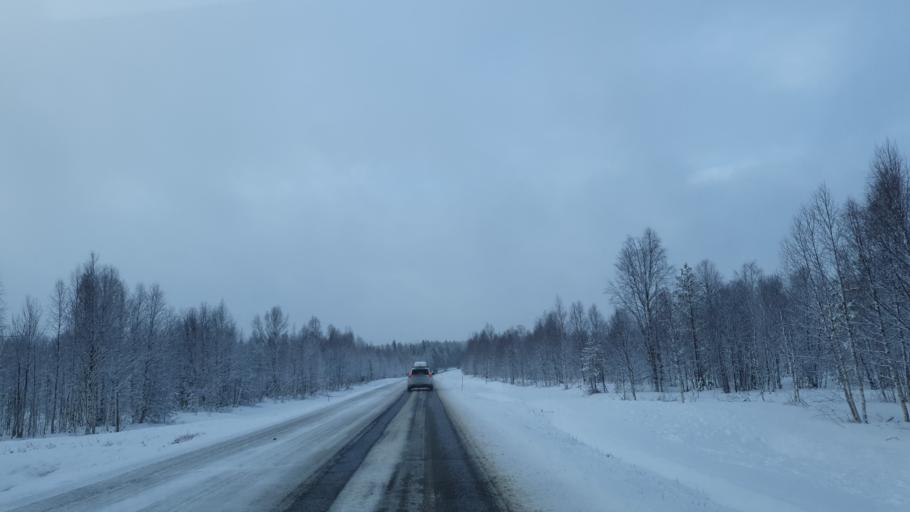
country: FI
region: Lapland
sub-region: Tunturi-Lappi
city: Kittilae
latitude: 67.4387
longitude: 24.9459
